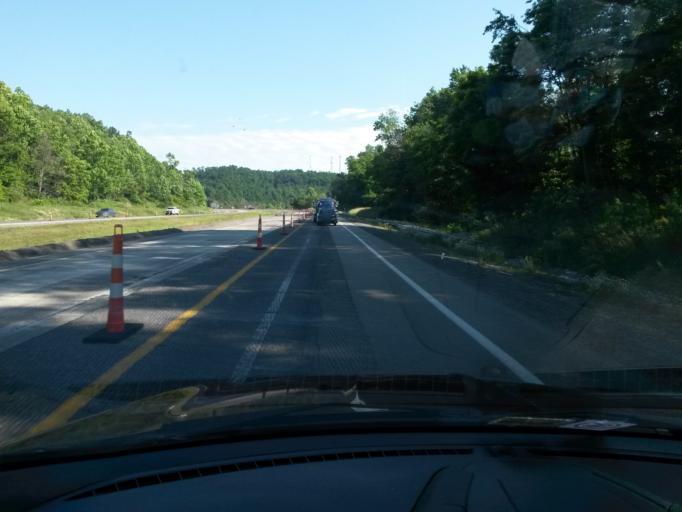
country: US
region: West Virginia
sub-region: Braxton County
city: Sutton
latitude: 38.7162
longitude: -80.6598
